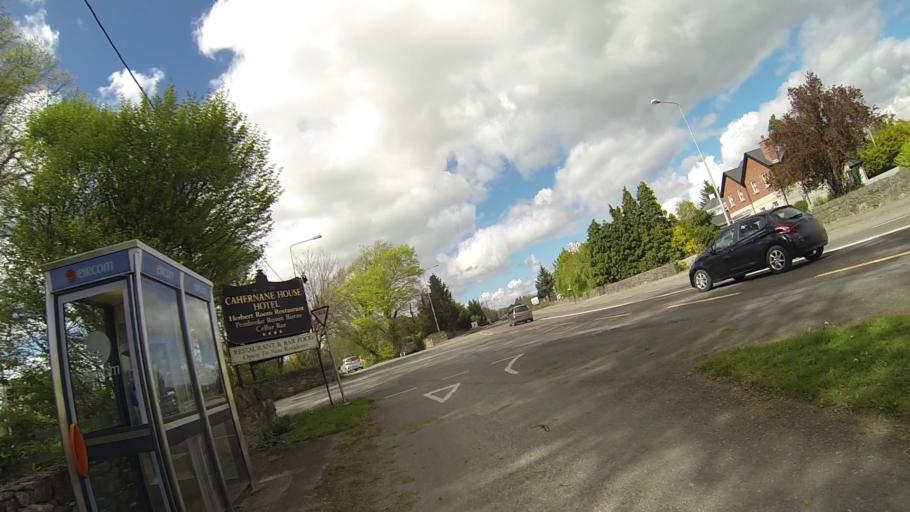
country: IE
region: Munster
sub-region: Ciarrai
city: Cill Airne
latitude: 52.0467
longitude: -9.5060
